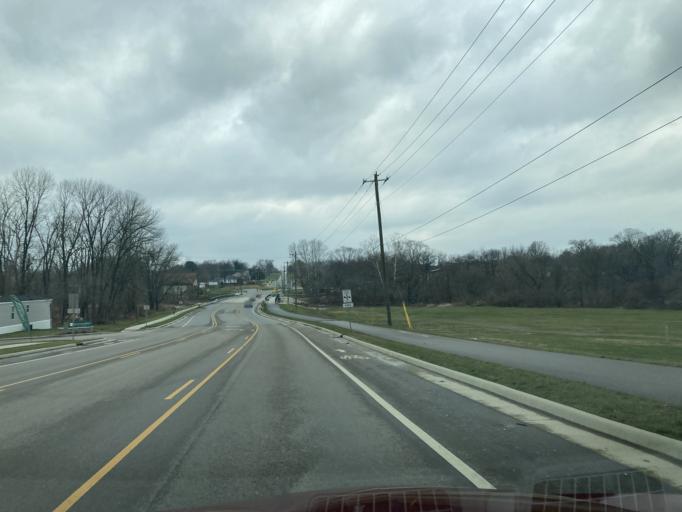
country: US
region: Indiana
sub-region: Monroe County
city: Bloomington
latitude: 39.1215
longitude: -86.5348
